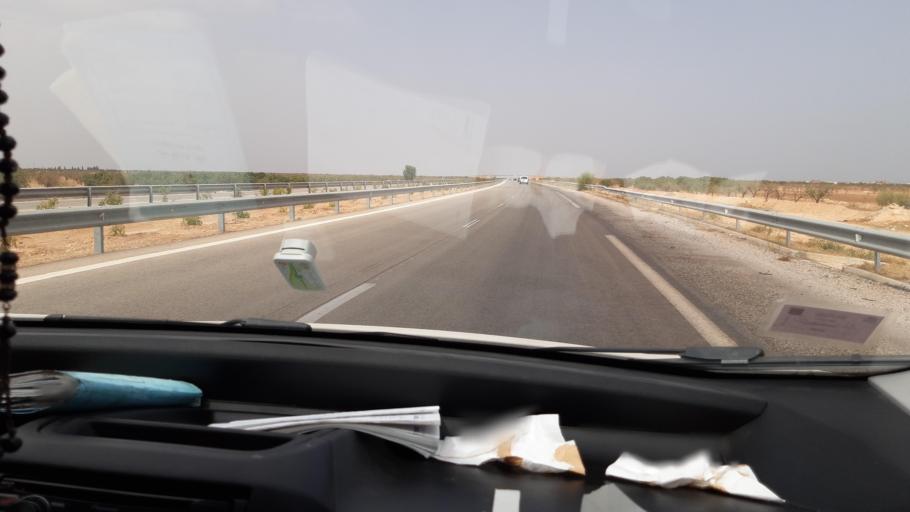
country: TN
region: Safaqis
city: Sfax
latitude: 34.8475
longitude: 10.6765
